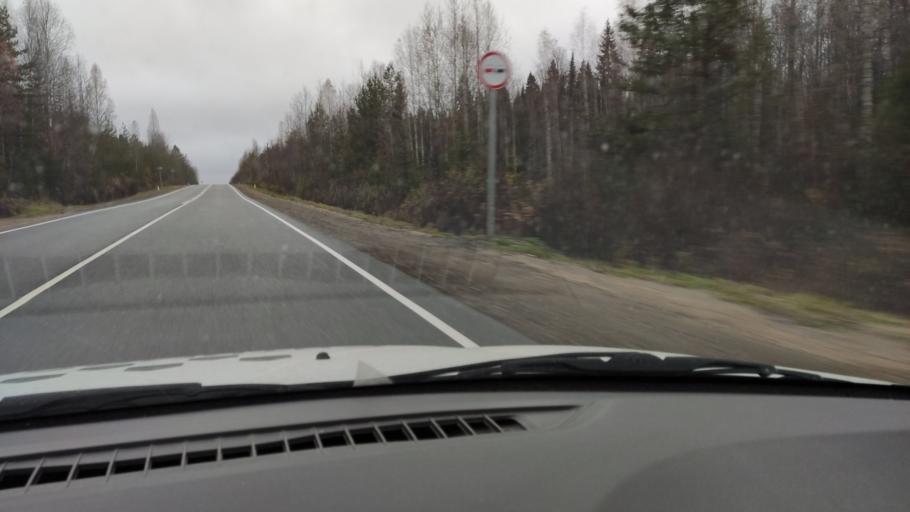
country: RU
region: Kirov
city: Omutninsk
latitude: 58.7160
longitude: 52.0917
